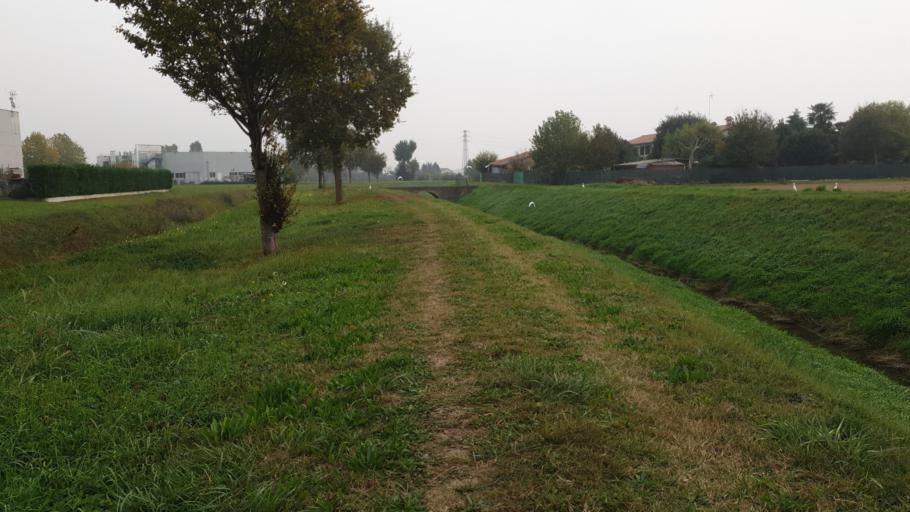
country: IT
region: Veneto
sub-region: Provincia di Padova
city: Casalserugo
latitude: 45.3067
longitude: 11.9111
